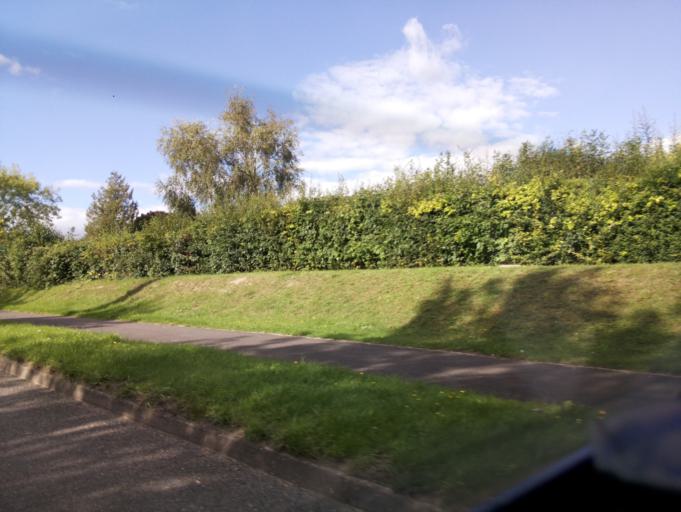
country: GB
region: England
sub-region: Hampshire
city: Compton
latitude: 51.0488
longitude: -1.3441
